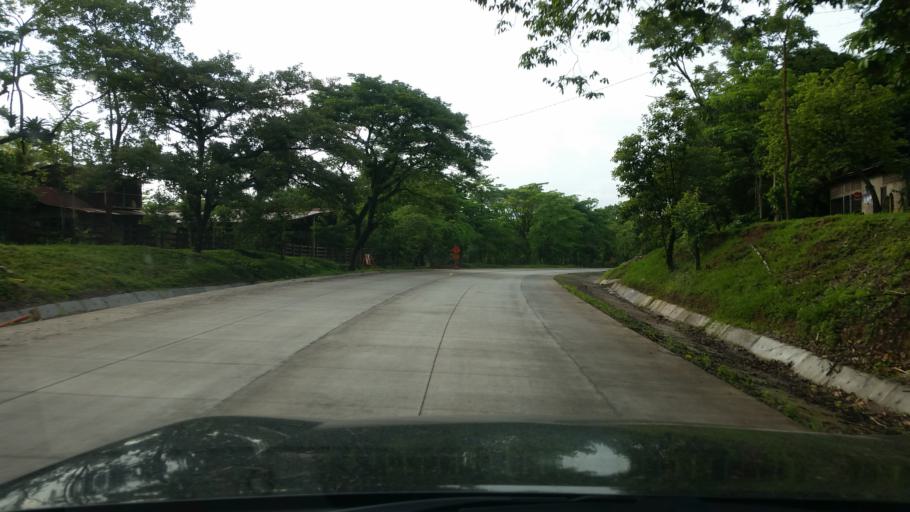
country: NI
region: Matagalpa
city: Rio Blanco
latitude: 13.1016
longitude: -85.0667
